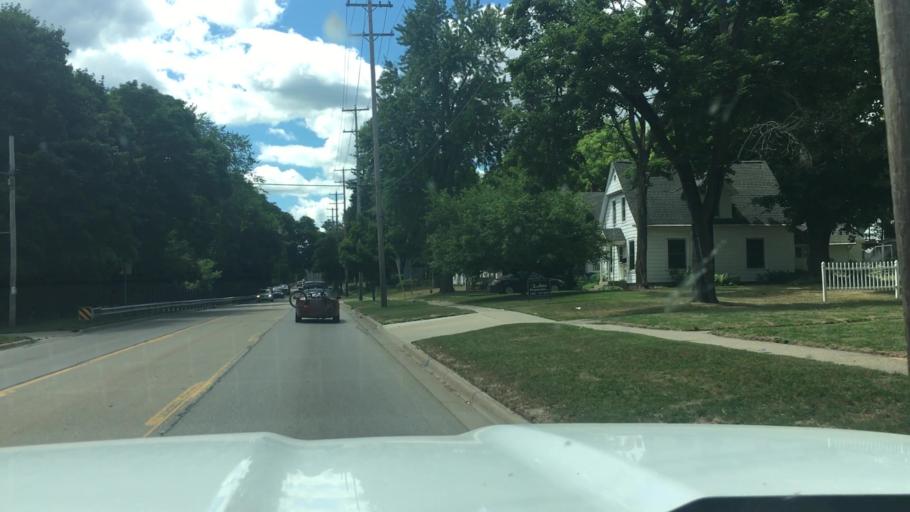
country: US
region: Michigan
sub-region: Montcalm County
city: Greenville
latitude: 43.1775
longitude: -85.2585
